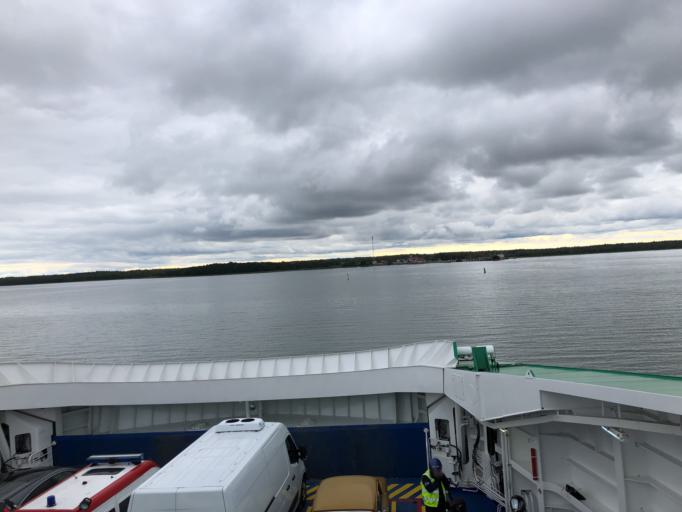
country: EE
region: Laeaene
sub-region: Vormsi vald
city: Hullo
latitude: 58.8683
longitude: 23.0668
